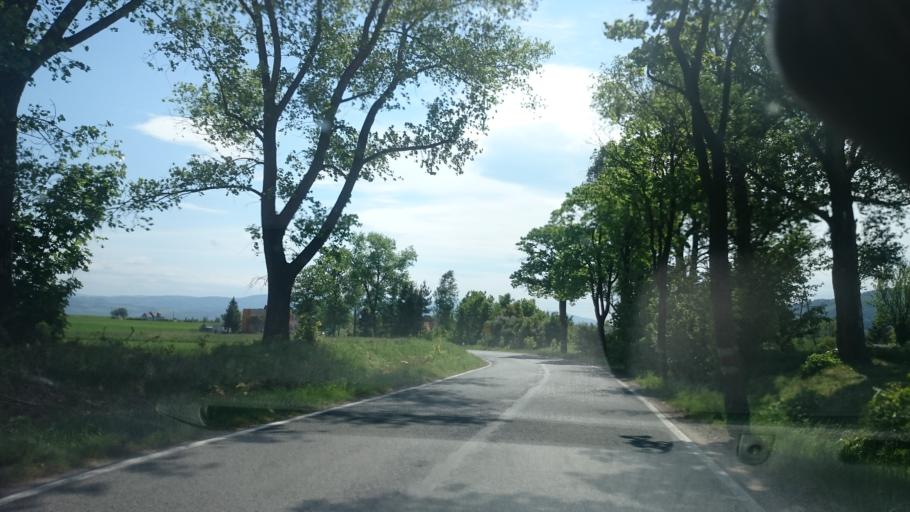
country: PL
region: Lower Silesian Voivodeship
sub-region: Powiat klodzki
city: Polanica-Zdroj
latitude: 50.3578
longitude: 16.5709
